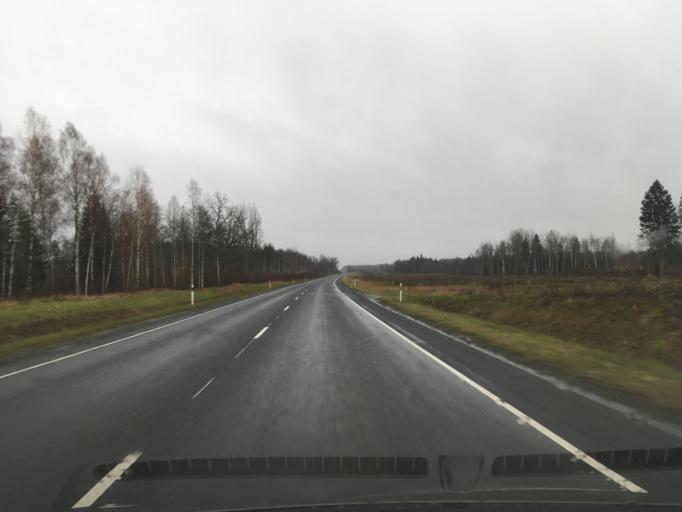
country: EE
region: Harju
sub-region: Nissi vald
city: Turba
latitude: 58.9508
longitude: 24.0821
